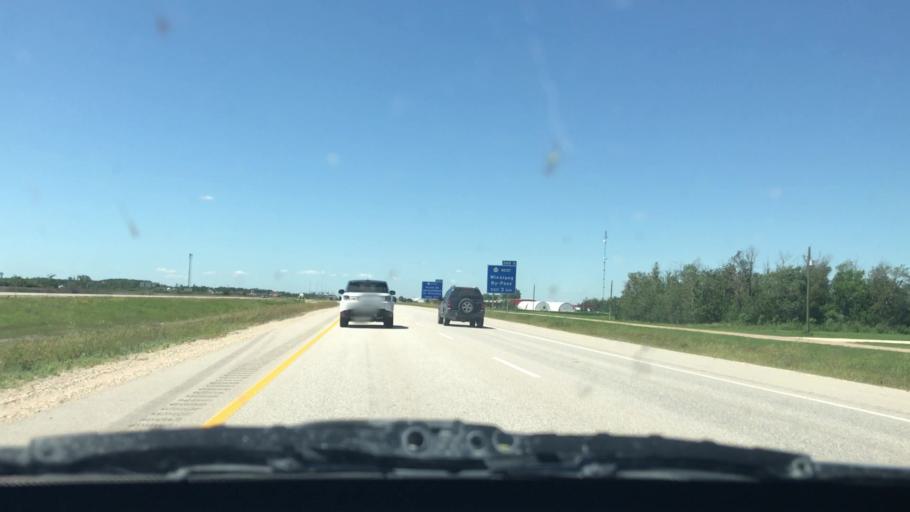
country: CA
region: Manitoba
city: Winnipeg
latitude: 49.8156
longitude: -96.9251
